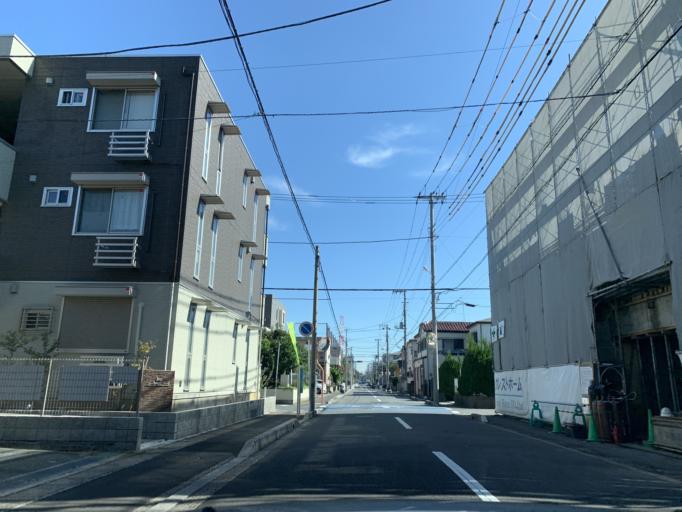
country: JP
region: Tokyo
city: Urayasu
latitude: 35.6553
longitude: 139.8896
